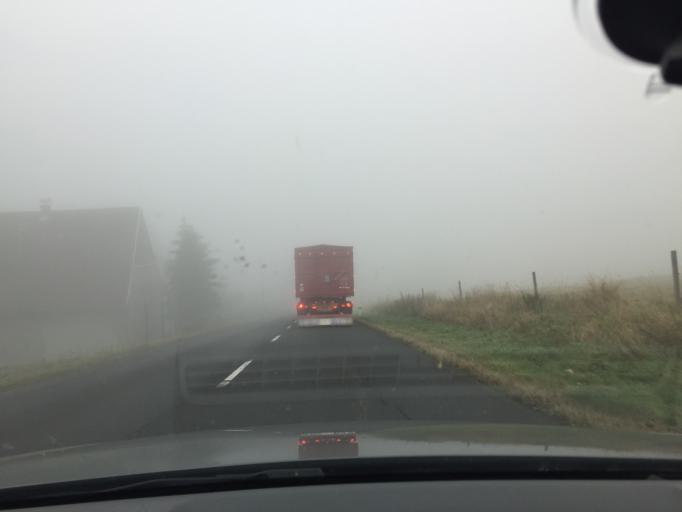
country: CZ
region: Ustecky
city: Libouchec
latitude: 50.7837
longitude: 13.9799
